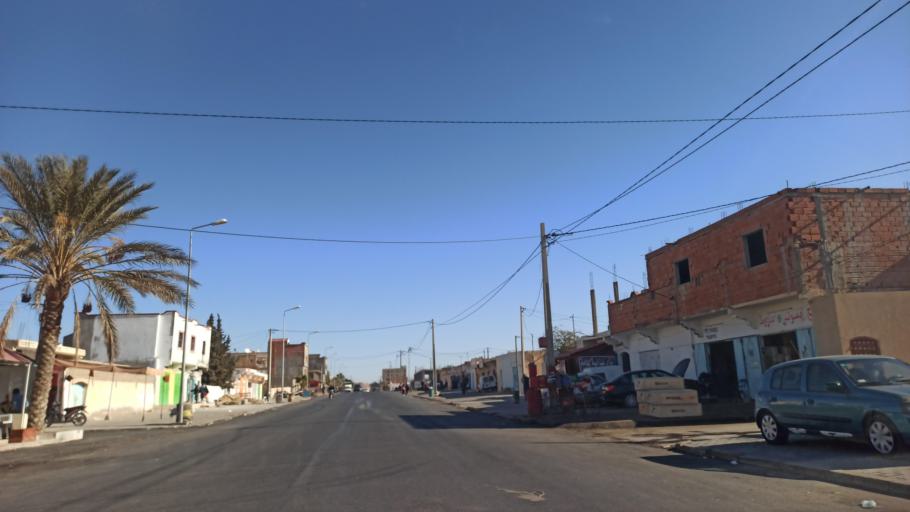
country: TN
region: Gafsa
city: Al Metlaoui
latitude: 34.3119
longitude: 8.3844
